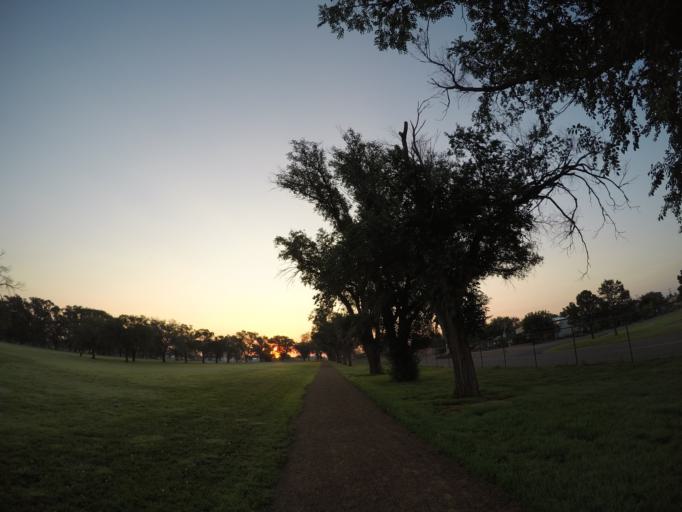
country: US
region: New Mexico
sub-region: Curry County
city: Clovis
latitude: 34.4050
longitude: -103.1818
